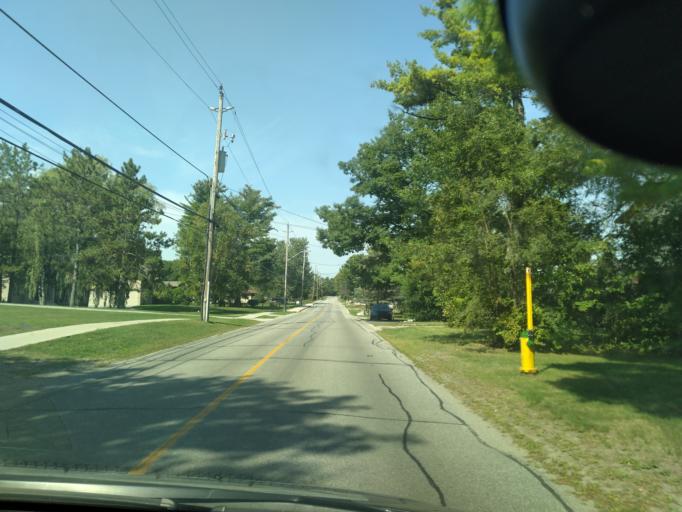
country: CA
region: Ontario
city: Newmarket
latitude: 44.1160
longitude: -79.5051
